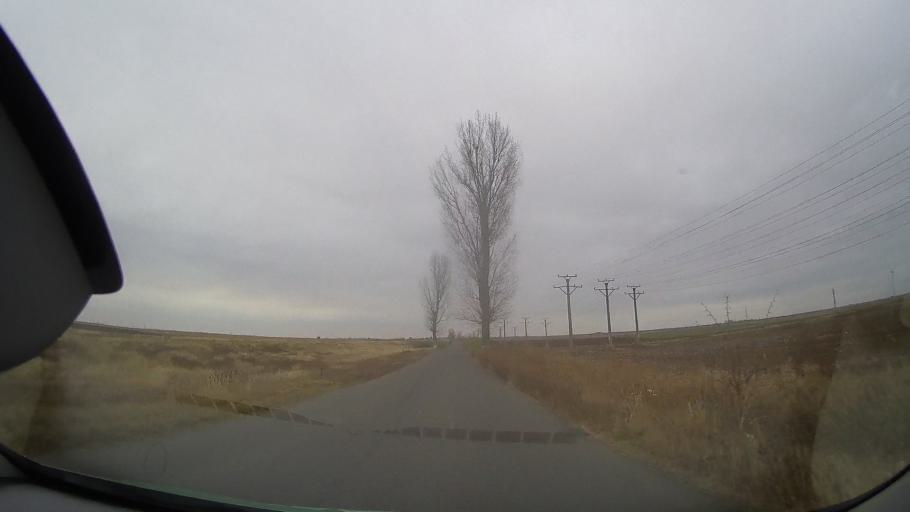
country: RO
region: Braila
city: Dudesti
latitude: 44.9072
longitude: 27.4313
